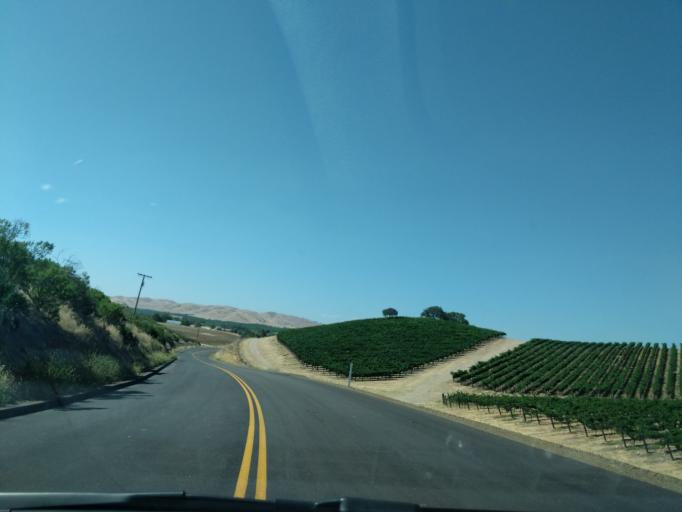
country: US
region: California
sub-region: San Luis Obispo County
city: San Miguel
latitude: 35.7045
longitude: -120.6401
